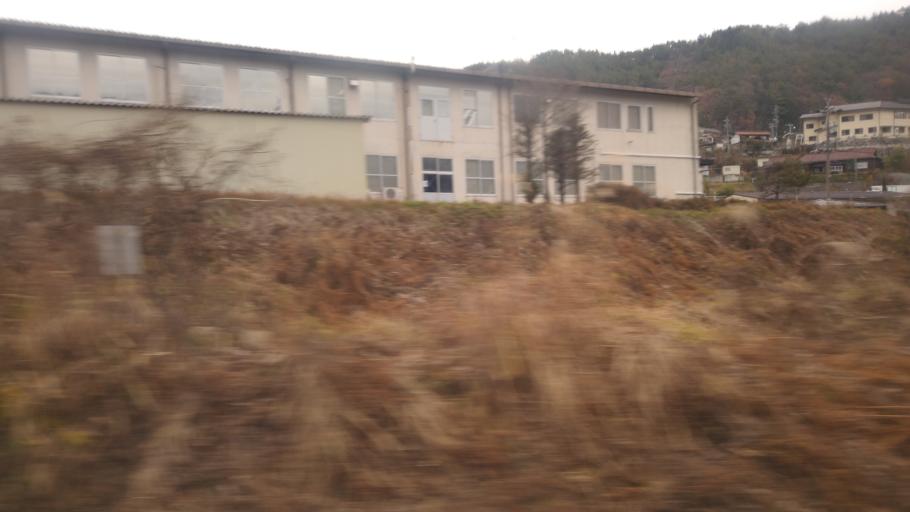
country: JP
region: Nagano
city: Ina
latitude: 35.7745
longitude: 137.6961
